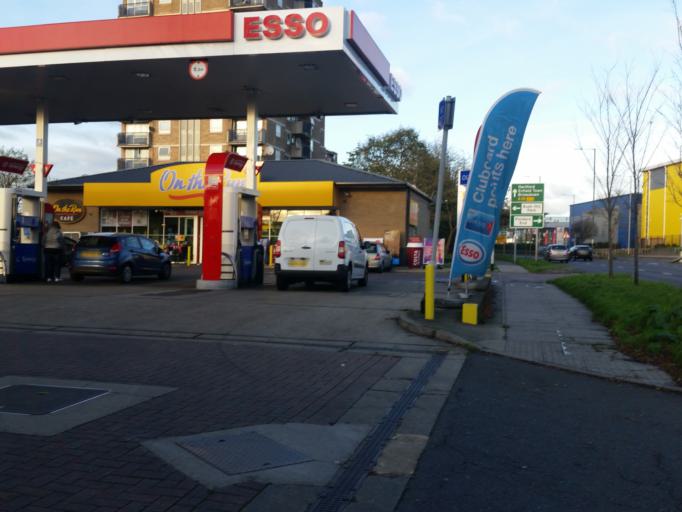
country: GB
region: England
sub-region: Greater London
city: Enfield
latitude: 51.6420
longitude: -0.0613
